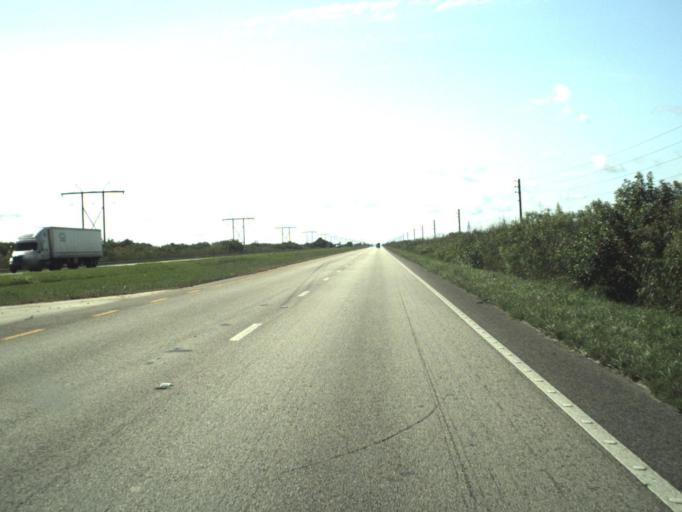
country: US
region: Florida
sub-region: Broward County
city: Weston
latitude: 26.3196
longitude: -80.5263
